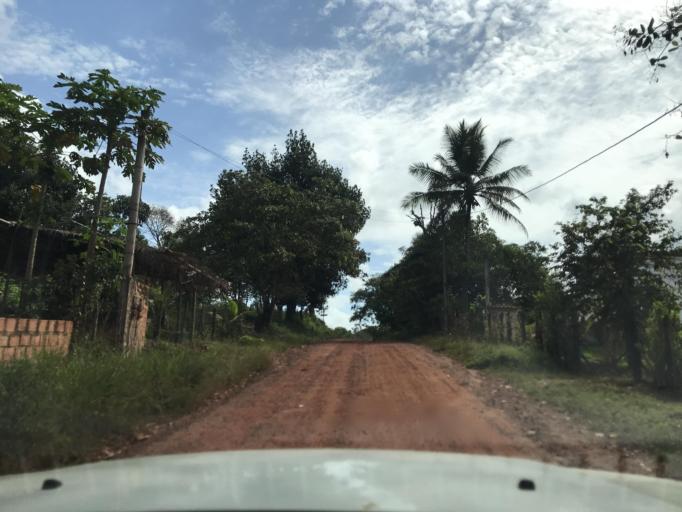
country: BR
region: Bahia
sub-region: Entre Rios
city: Entre Rios
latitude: -12.1755
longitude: -38.1182
